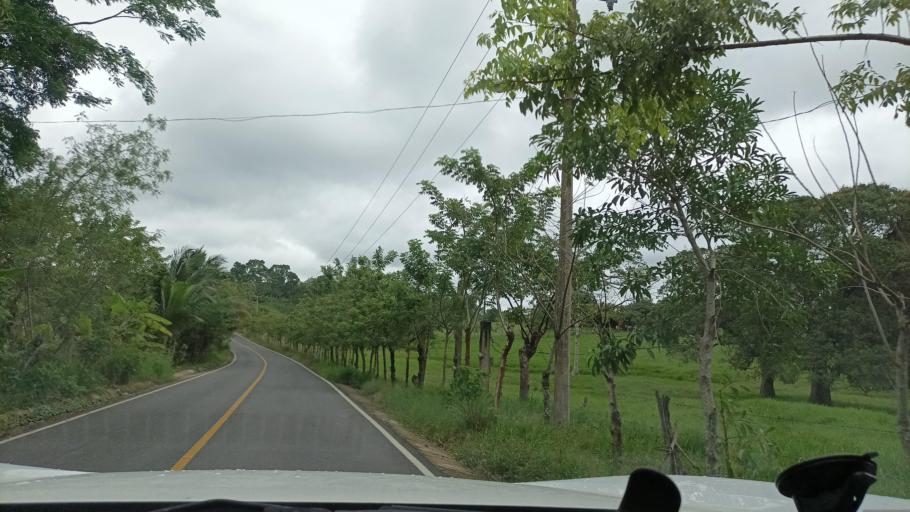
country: MX
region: Veracruz
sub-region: Moloacan
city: Cuichapa
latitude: 17.8007
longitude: -94.3579
